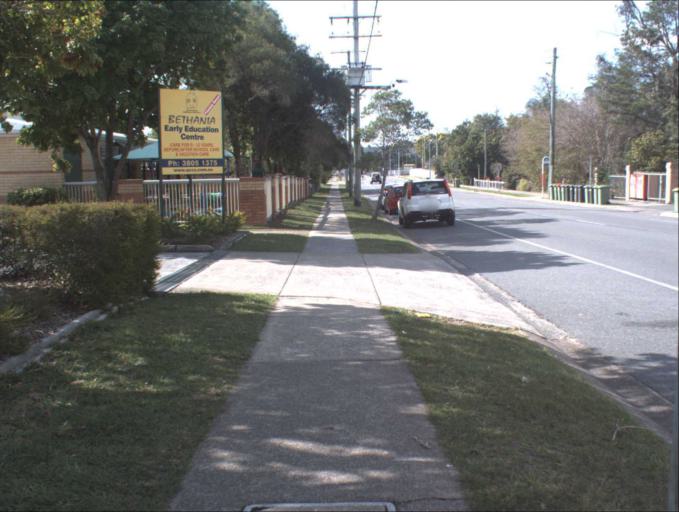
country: AU
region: Queensland
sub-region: Logan
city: Waterford West
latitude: -27.6895
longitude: 153.1571
